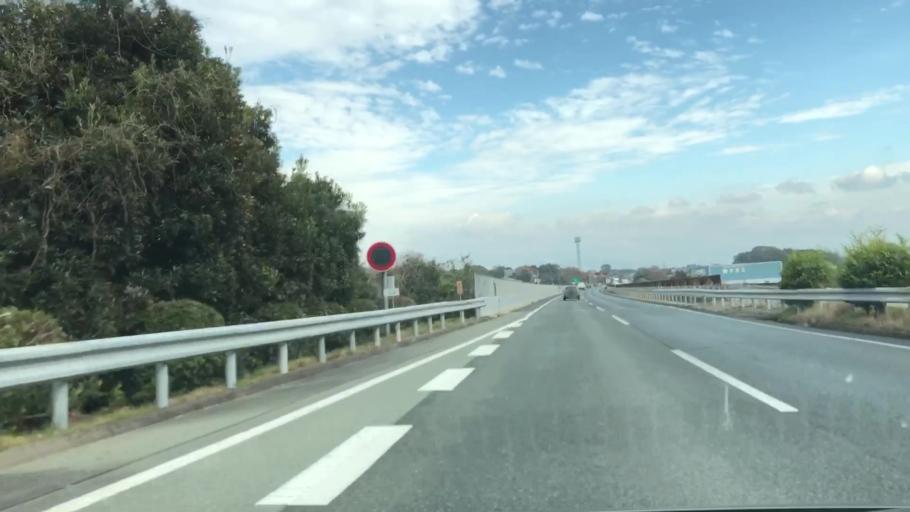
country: JP
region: Saga Prefecture
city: Tosu
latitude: 33.3957
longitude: 130.5034
